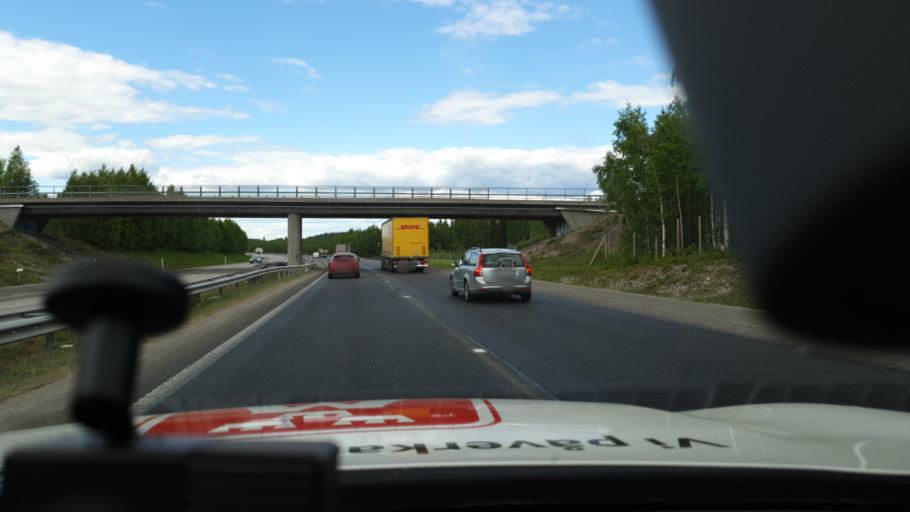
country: SE
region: Norrbotten
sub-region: Pitea Kommun
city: Pitea
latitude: 65.3500
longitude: 21.4379
